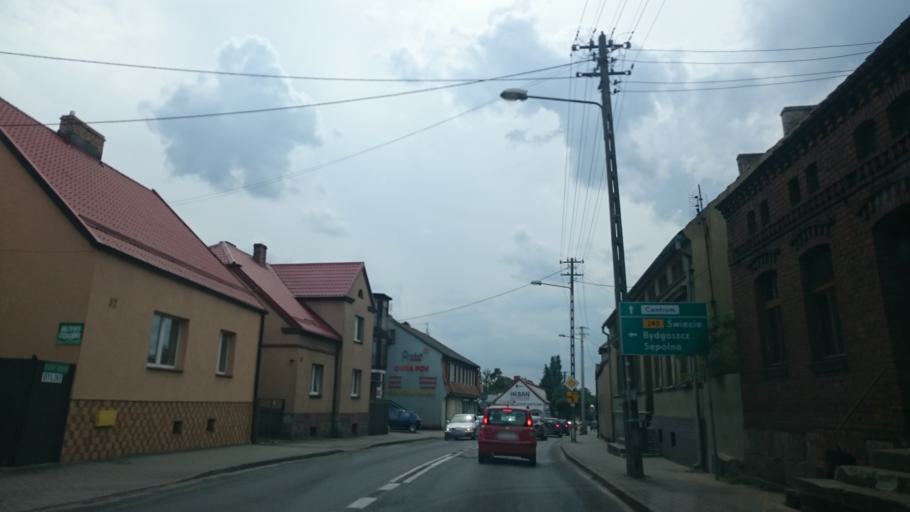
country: PL
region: Kujawsko-Pomorskie
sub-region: Powiat tucholski
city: Tuchola
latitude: 53.5914
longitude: 17.8656
